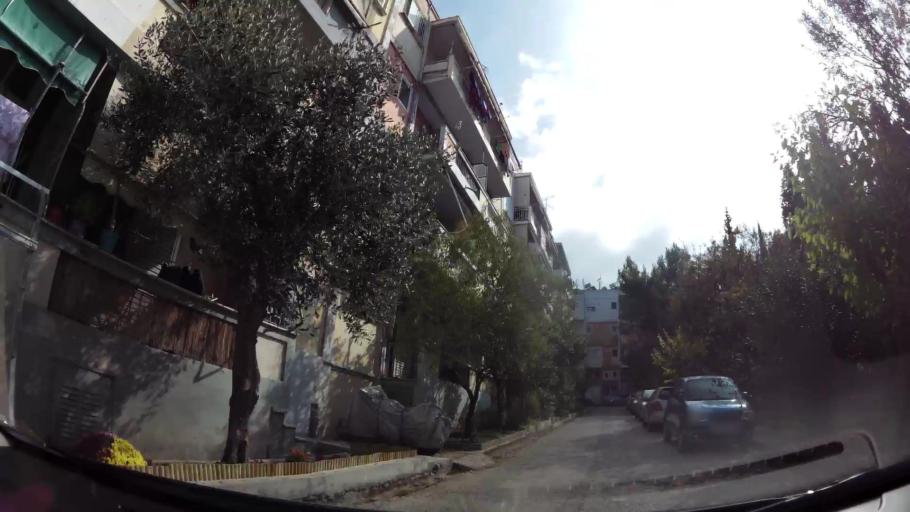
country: GR
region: Attica
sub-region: Nomarchia Athinas
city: Kaisariani
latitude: 37.9484
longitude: 23.7720
